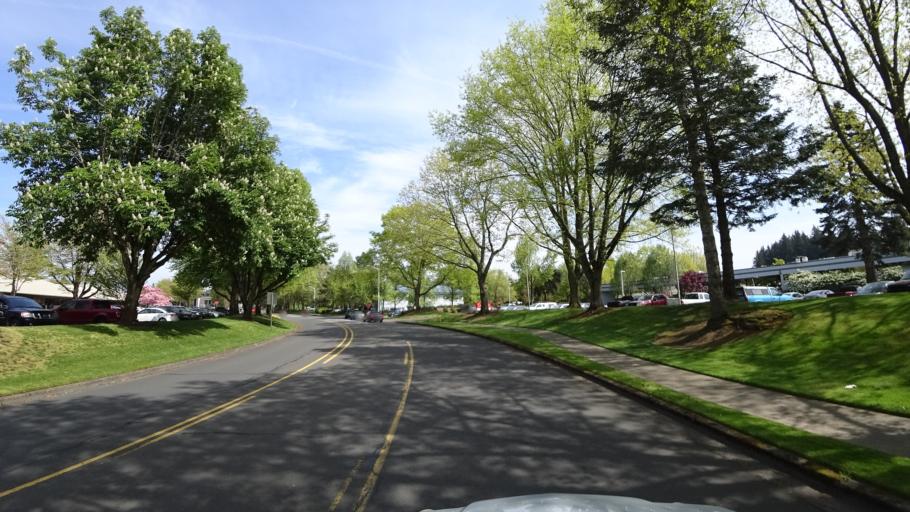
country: US
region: Oregon
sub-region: Washington County
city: Rockcreek
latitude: 45.5272
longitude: -122.9303
